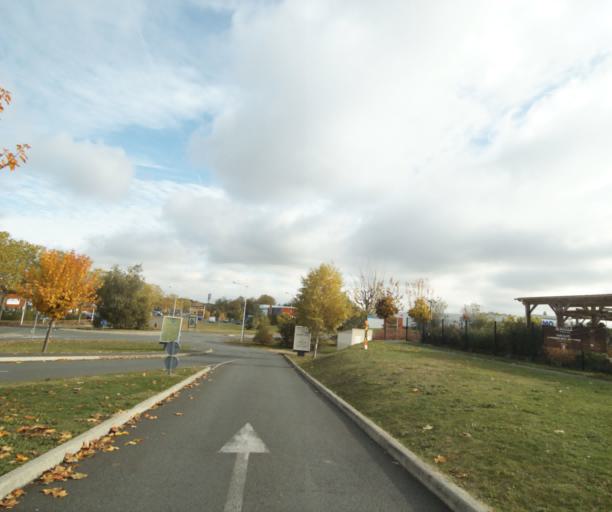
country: FR
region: Poitou-Charentes
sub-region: Departement de la Charente-Maritime
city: Saint-Georges-des-Coteaux
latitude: 45.7491
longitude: -0.6774
